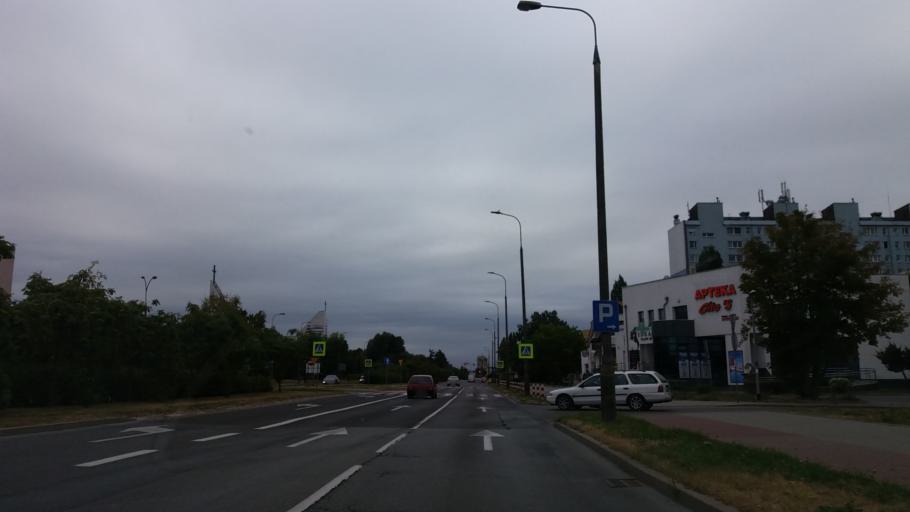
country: PL
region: Lubusz
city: Gorzow Wielkopolski
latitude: 52.7521
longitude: 15.2443
